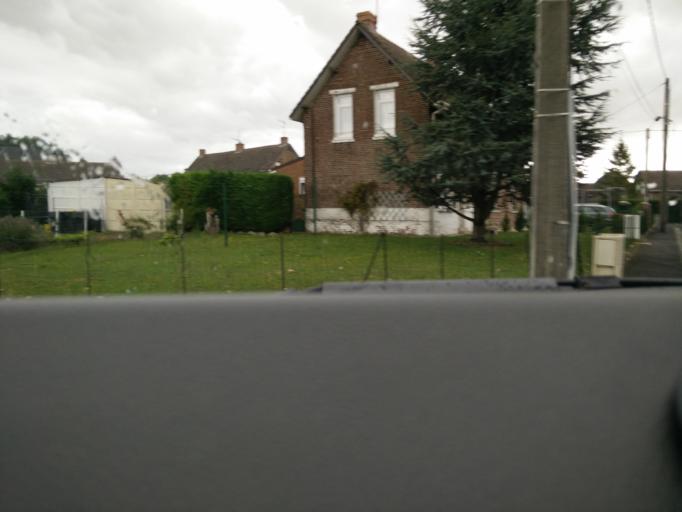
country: FR
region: Nord-Pas-de-Calais
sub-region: Departement du Pas-de-Calais
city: Grenay
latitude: 50.4537
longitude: 2.7467
